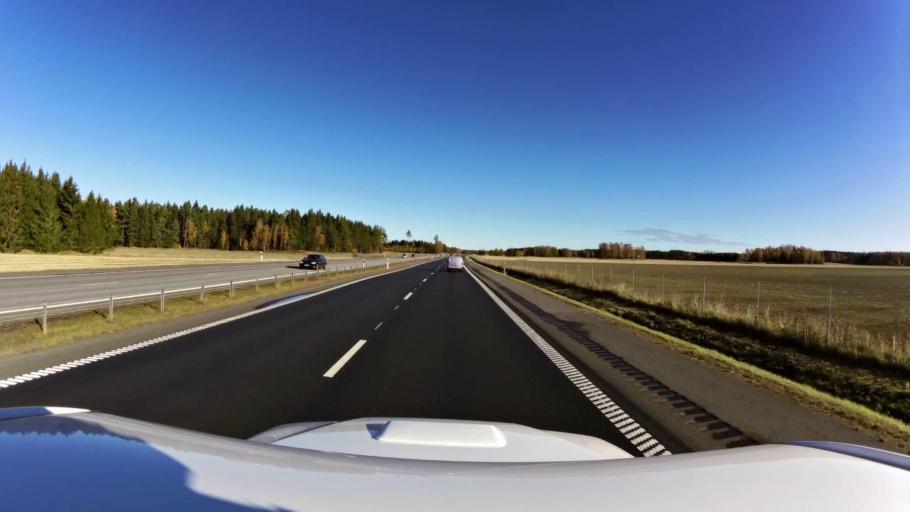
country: SE
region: OEstergoetland
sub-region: Linkopings Kommun
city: Vikingstad
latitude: 58.4022
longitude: 15.4397
